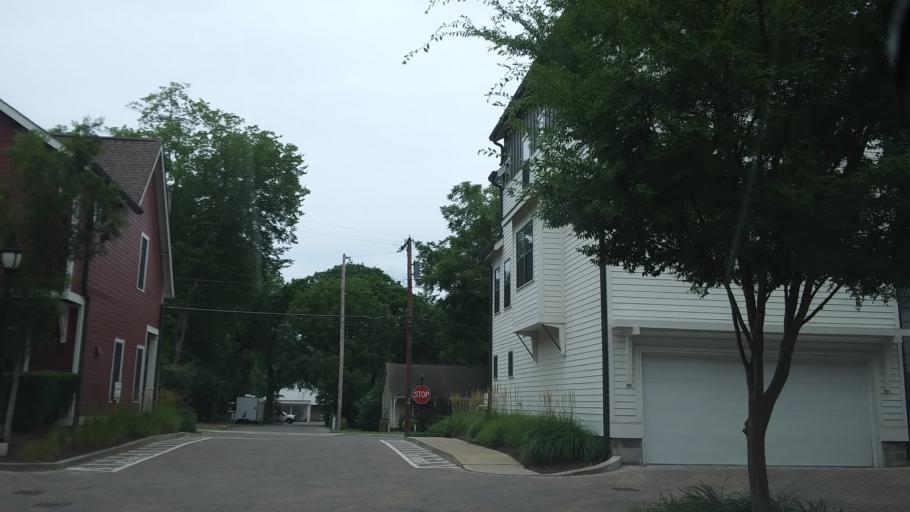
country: US
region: Tennessee
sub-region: Davidson County
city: Belle Meade
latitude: 36.1503
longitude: -86.8529
